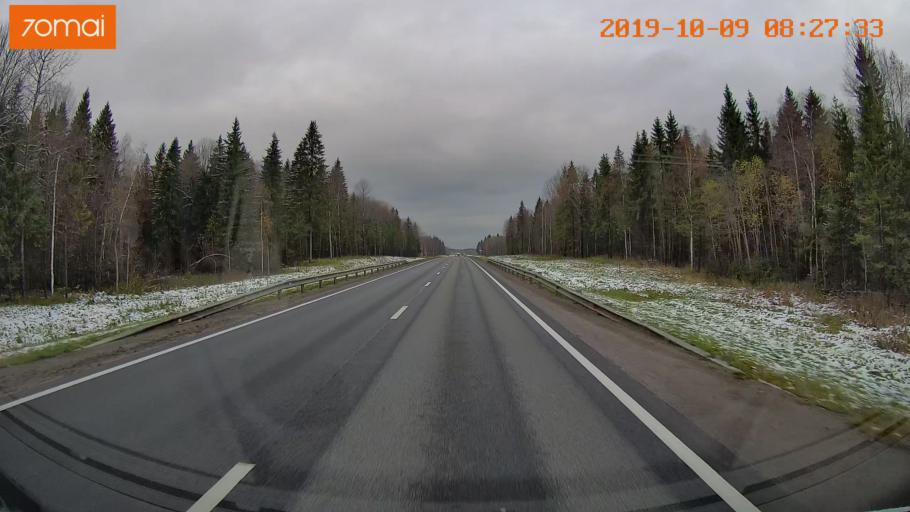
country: RU
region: Vologda
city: Gryazovets
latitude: 58.8051
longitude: 40.2470
